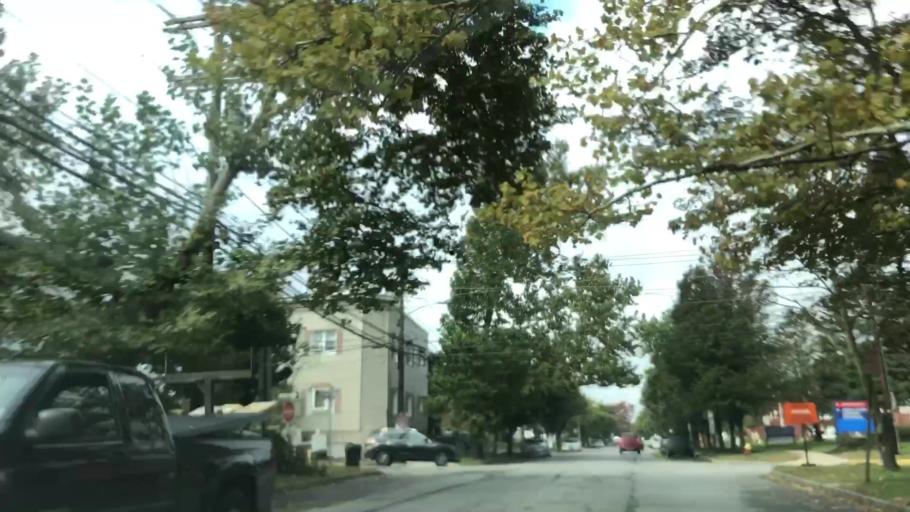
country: US
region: New Jersey
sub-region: Essex County
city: Bloomfield
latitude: 40.7840
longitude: -74.1778
